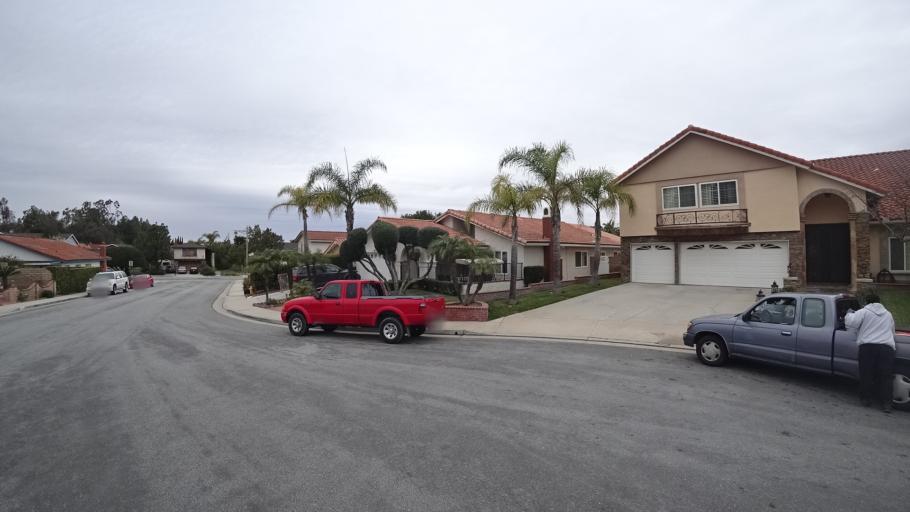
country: US
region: California
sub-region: Orange County
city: Villa Park
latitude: 33.8321
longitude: -117.7588
